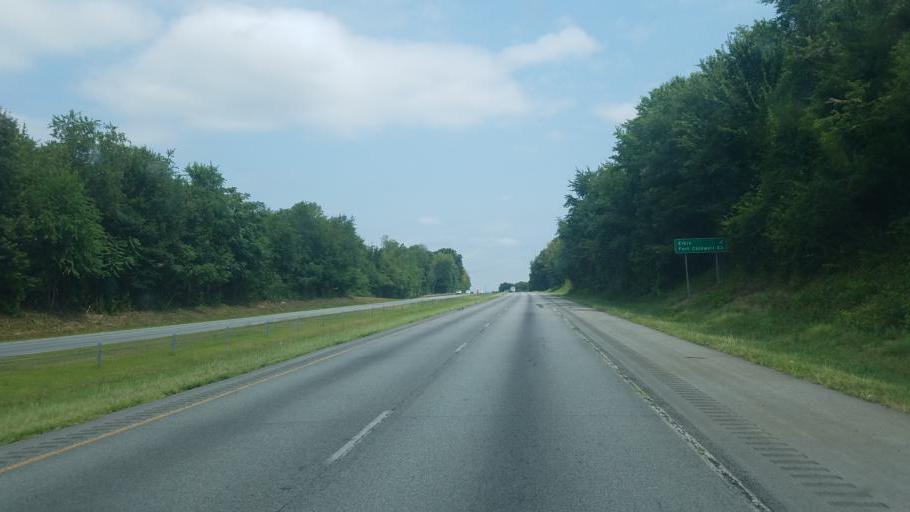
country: US
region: North Carolina
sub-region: Yadkin County
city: Jonesville
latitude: 36.2054
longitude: -80.8108
